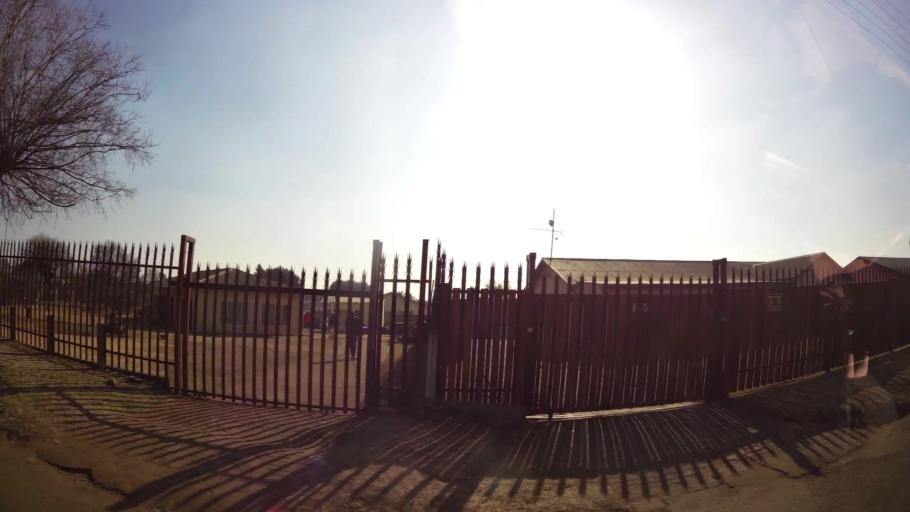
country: ZA
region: Gauteng
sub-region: West Rand District Municipality
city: Randfontein
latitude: -26.1827
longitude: 27.6952
